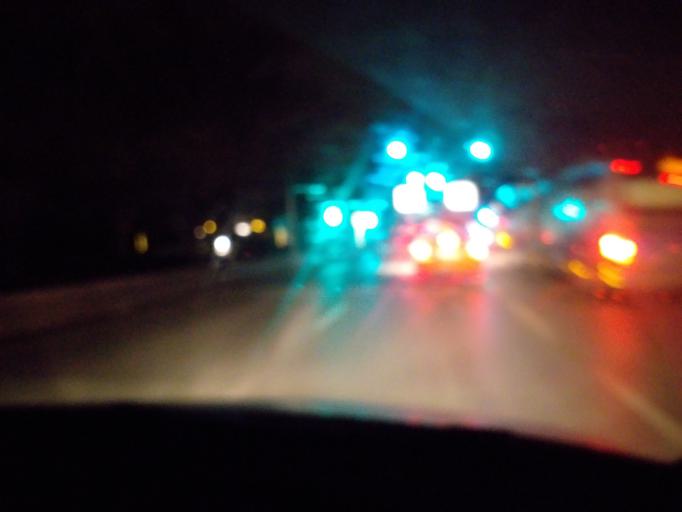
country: TR
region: Ankara
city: Batikent
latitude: 39.9044
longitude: 32.7329
